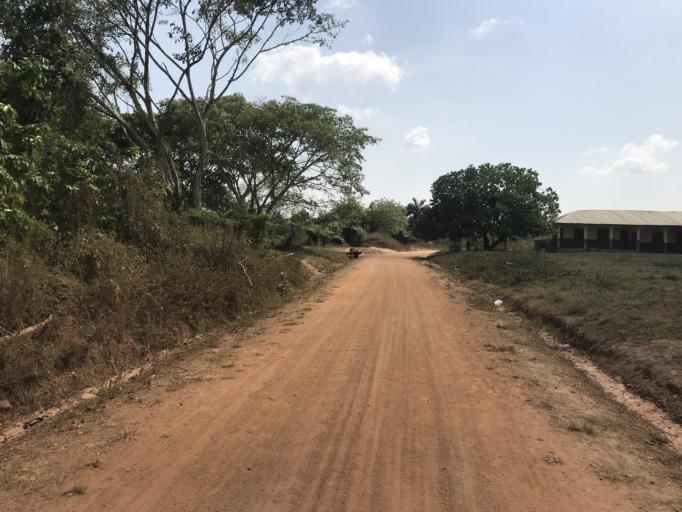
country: NG
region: Osun
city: Ifon
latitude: 7.9517
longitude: 4.4932
